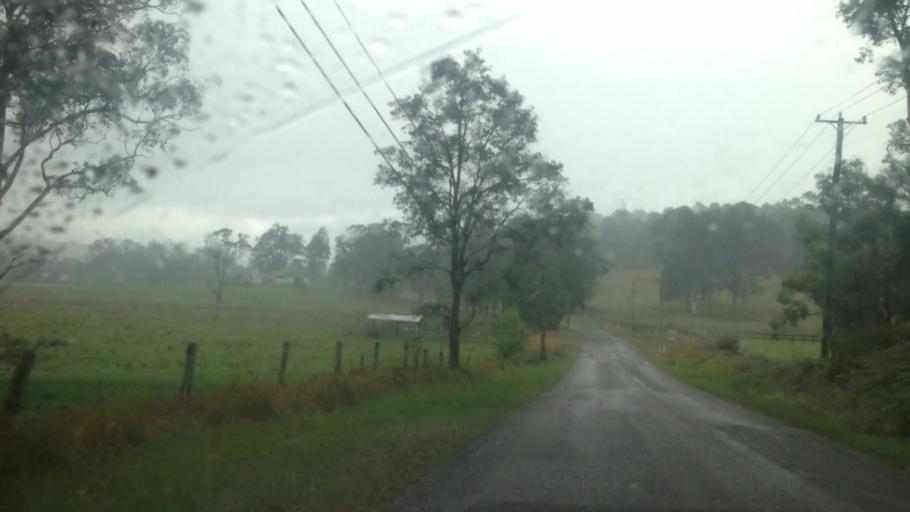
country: AU
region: New South Wales
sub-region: Wyong Shire
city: Little Jilliby
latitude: -33.1940
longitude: 151.3572
